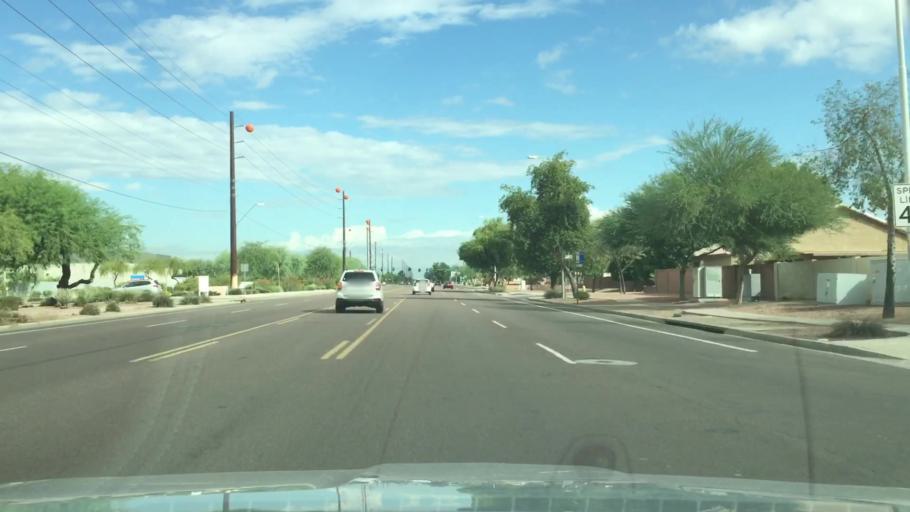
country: US
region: Arizona
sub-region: Maricopa County
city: Tolleson
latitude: 33.4764
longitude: -112.2552
